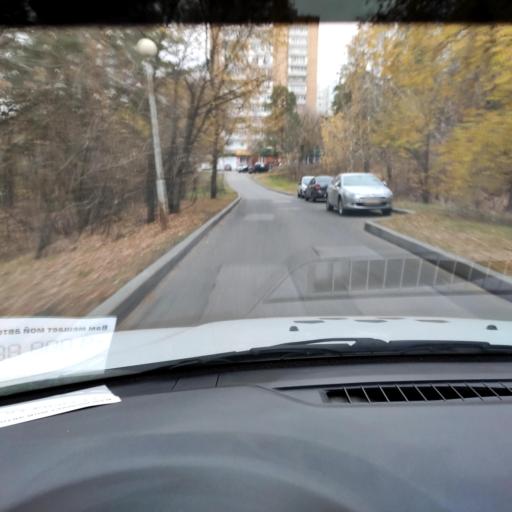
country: RU
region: Samara
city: Zhigulevsk
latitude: 53.4872
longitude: 49.4660
